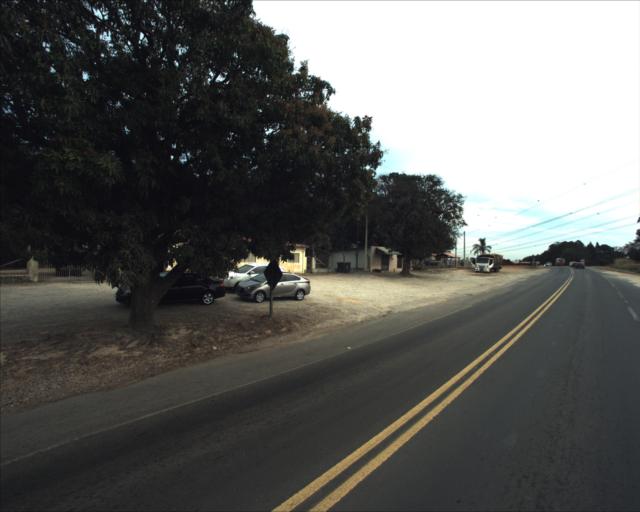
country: BR
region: Sao Paulo
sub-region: Sorocaba
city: Sorocaba
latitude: -23.3830
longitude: -47.5169
